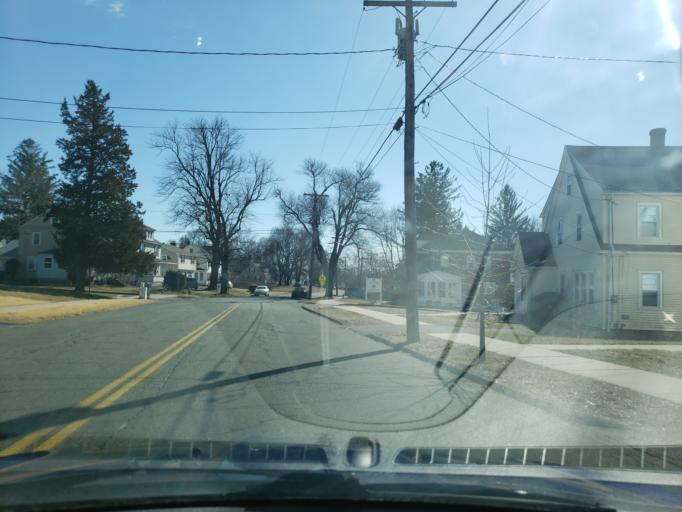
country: US
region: Connecticut
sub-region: Hartford County
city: Thompsonville
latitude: 41.9880
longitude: -72.5976
